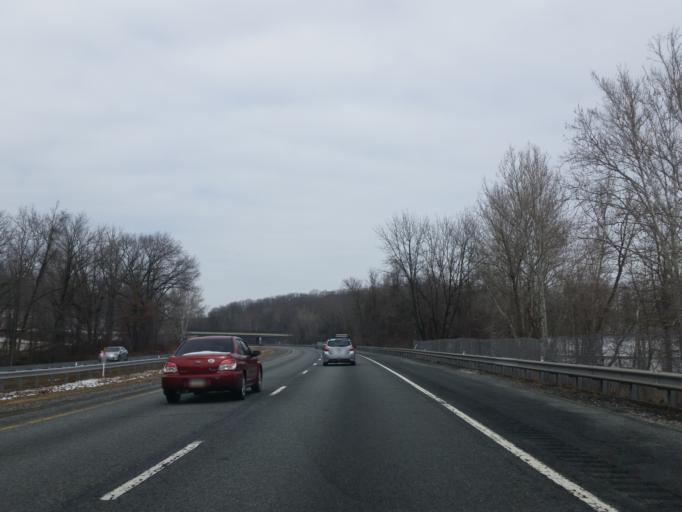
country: US
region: Maryland
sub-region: Baltimore County
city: Hunt Valley
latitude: 39.5597
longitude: -76.6647
